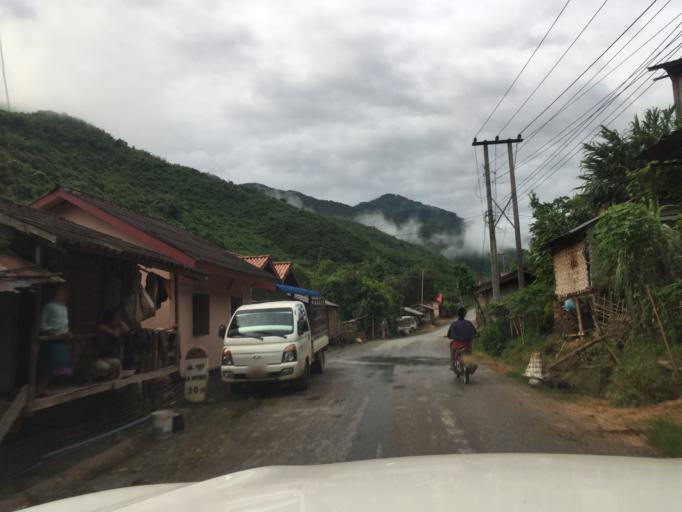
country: LA
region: Oudomxai
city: Muang La
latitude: 21.0532
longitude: 102.2409
